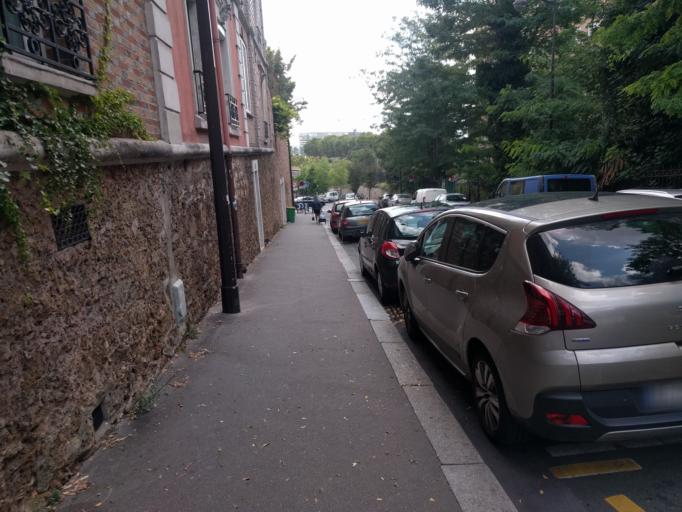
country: FR
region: Ile-de-France
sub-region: Departement du Val-de-Marne
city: Ivry-sur-Seine
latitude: 48.8240
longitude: 2.3748
